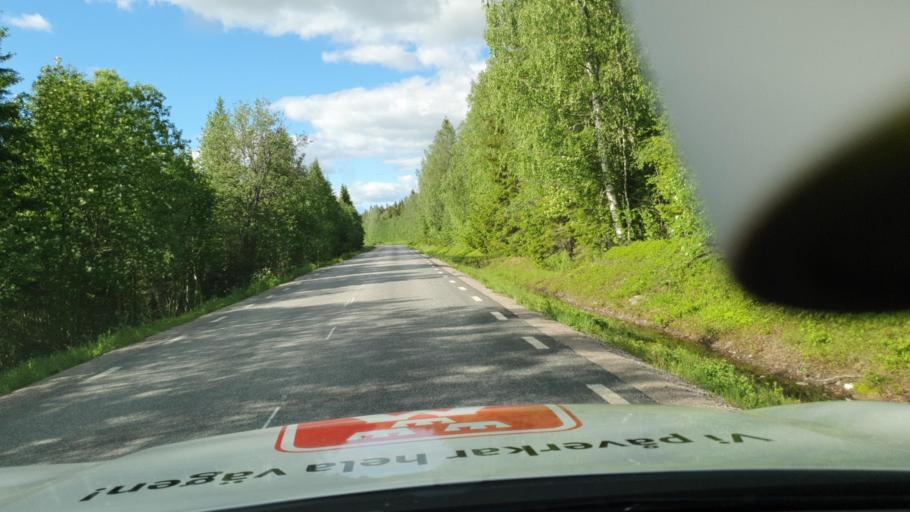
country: SE
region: Vaesterbotten
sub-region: Vannas Kommun
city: Vannasby
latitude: 63.8263
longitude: 19.8569
